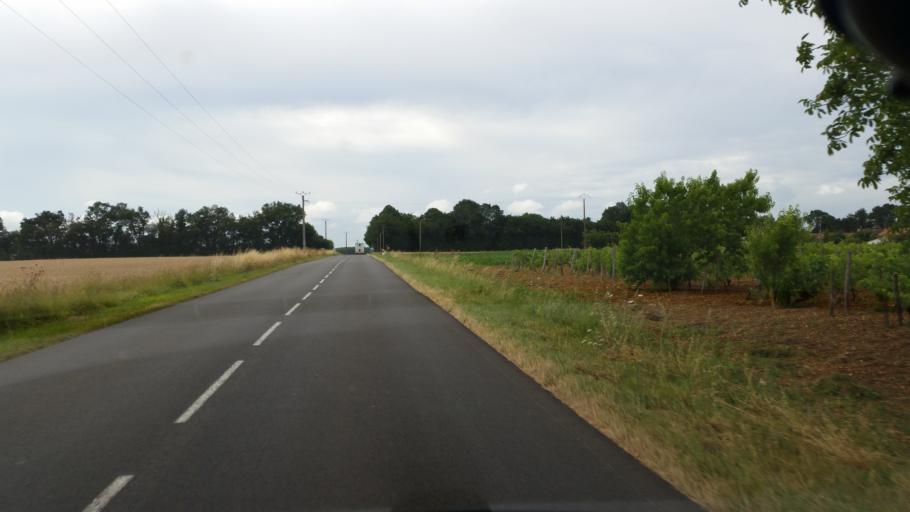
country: FR
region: Poitou-Charentes
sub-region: Departement de la Charente-Maritime
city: Saint-Germain-de-Marencennes
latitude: 46.1563
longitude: -0.8215
